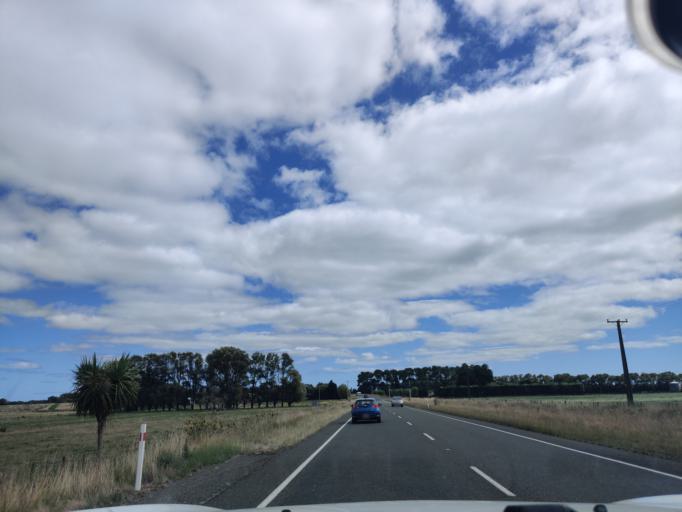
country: NZ
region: Manawatu-Wanganui
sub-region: Horowhenua District
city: Foxton
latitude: -40.4244
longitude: 175.4517
